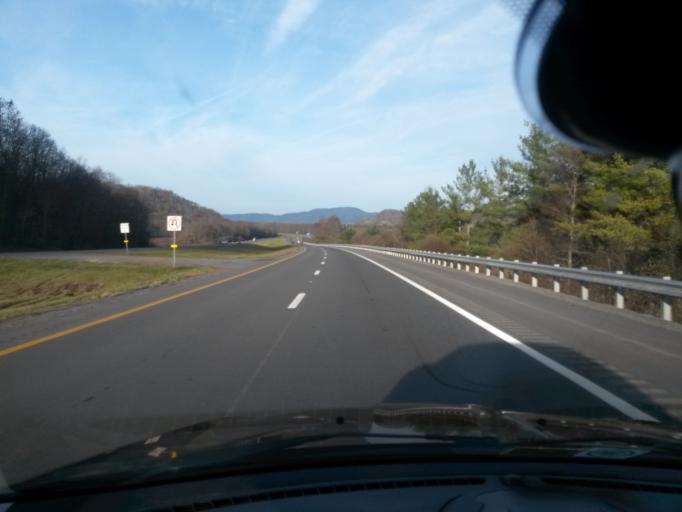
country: US
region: West Virginia
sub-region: Greenbrier County
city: Rainelle
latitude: 37.9049
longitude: -80.6002
